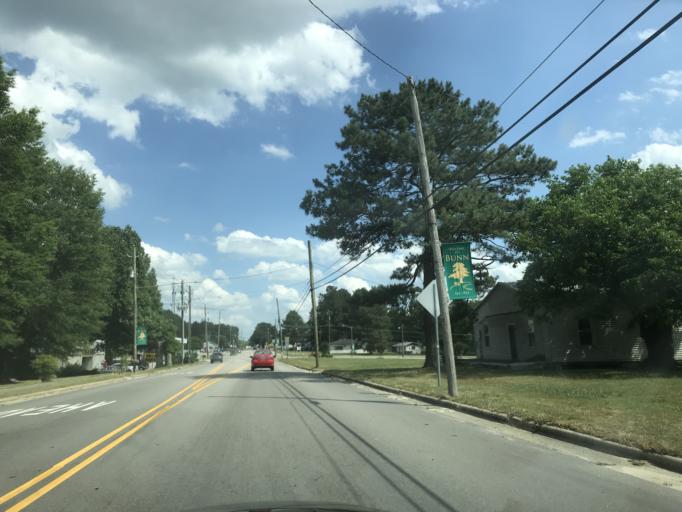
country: US
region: North Carolina
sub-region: Nash County
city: Spring Hope
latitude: 35.9594
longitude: -78.2522
